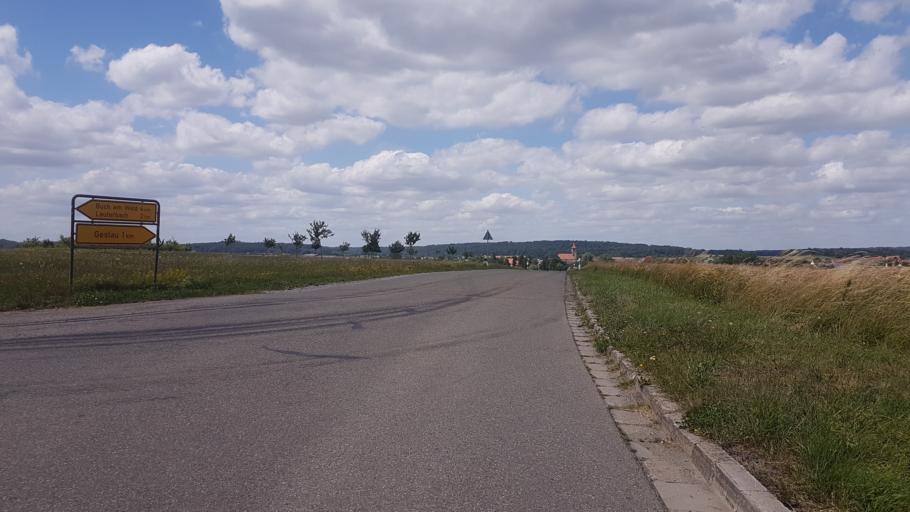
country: DE
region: Bavaria
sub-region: Regierungsbezirk Mittelfranken
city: Geslau
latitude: 49.3591
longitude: 10.3153
